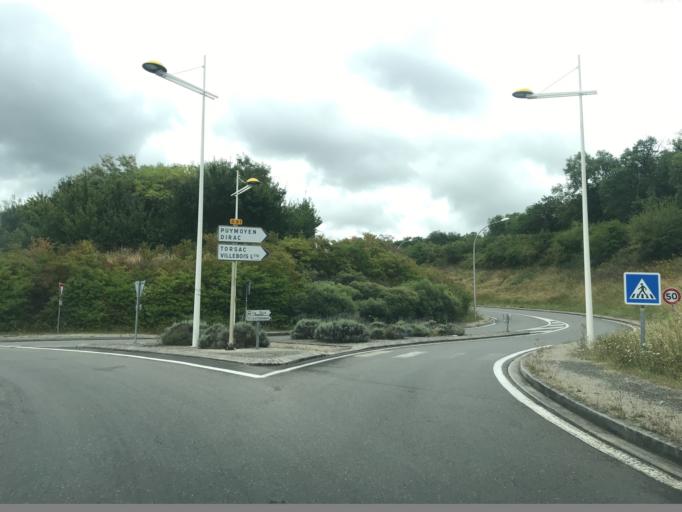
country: FR
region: Poitou-Charentes
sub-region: Departement de la Charente
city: Puymoyen
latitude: 45.6252
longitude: 0.1798
